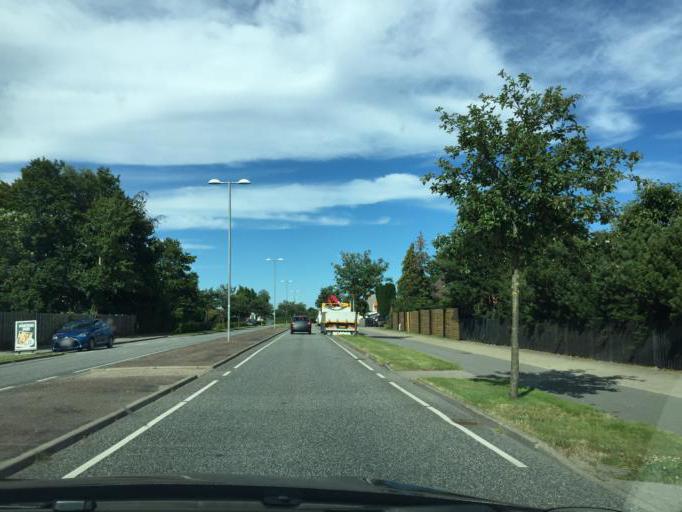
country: DK
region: Zealand
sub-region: Solrod Kommune
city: Solrod Strand
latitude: 55.5239
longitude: 12.2157
